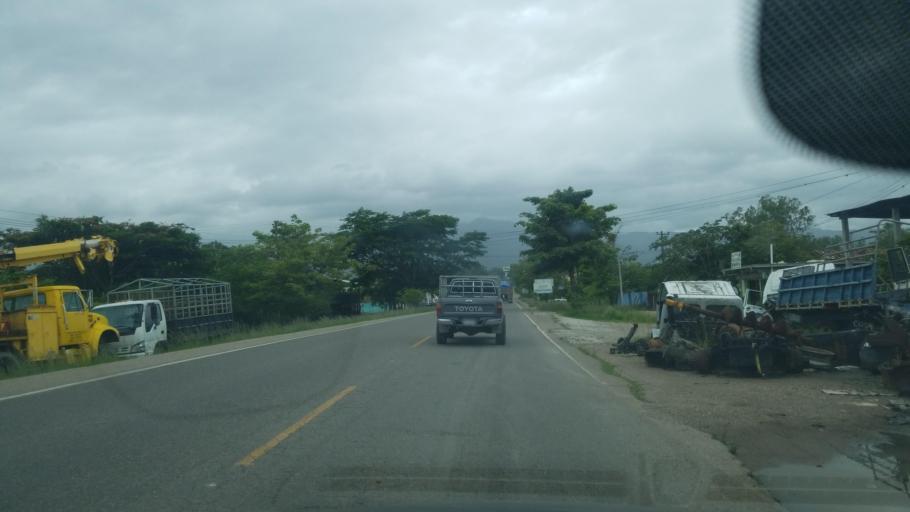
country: HN
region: Ocotepeque
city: Sensenti
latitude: 14.5120
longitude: -88.9544
